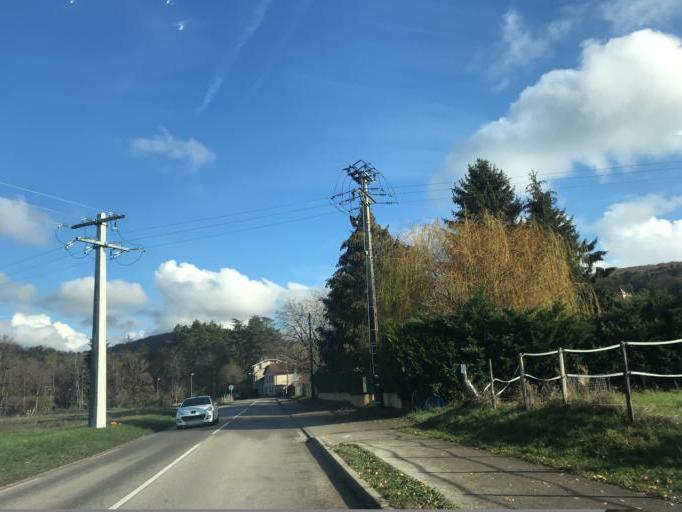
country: FR
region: Rhone-Alpes
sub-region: Departement de l'Ain
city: Saint-Jean-le-Vieux
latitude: 46.0341
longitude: 5.4007
